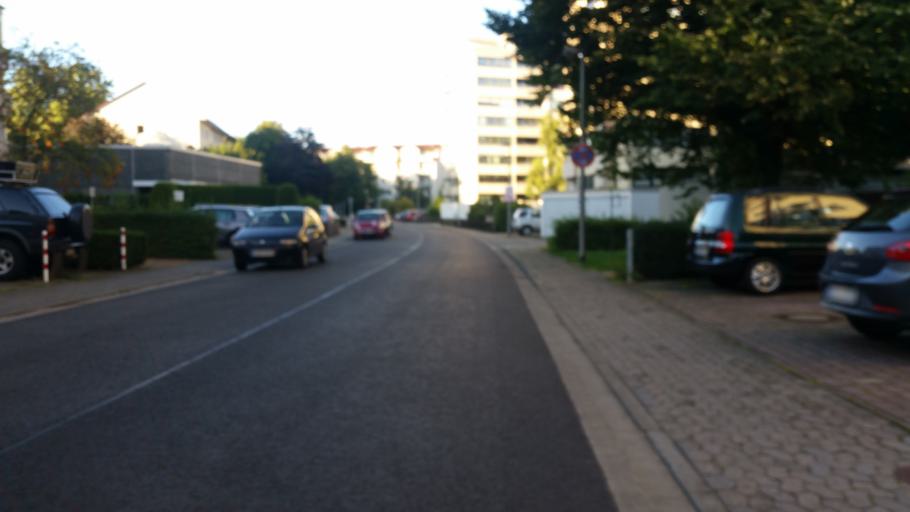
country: DE
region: Lower Saxony
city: Isernhagen Farster Bauerschaft
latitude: 52.3945
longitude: 9.8607
